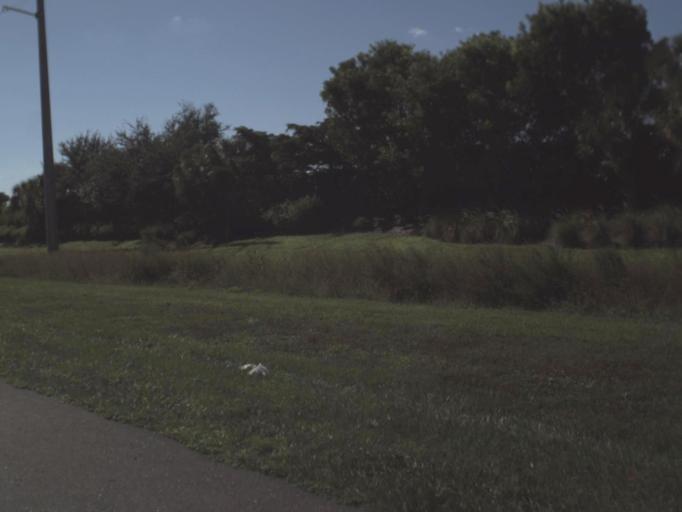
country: US
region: Florida
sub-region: Lee County
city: Gateway
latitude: 26.6043
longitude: -81.7514
